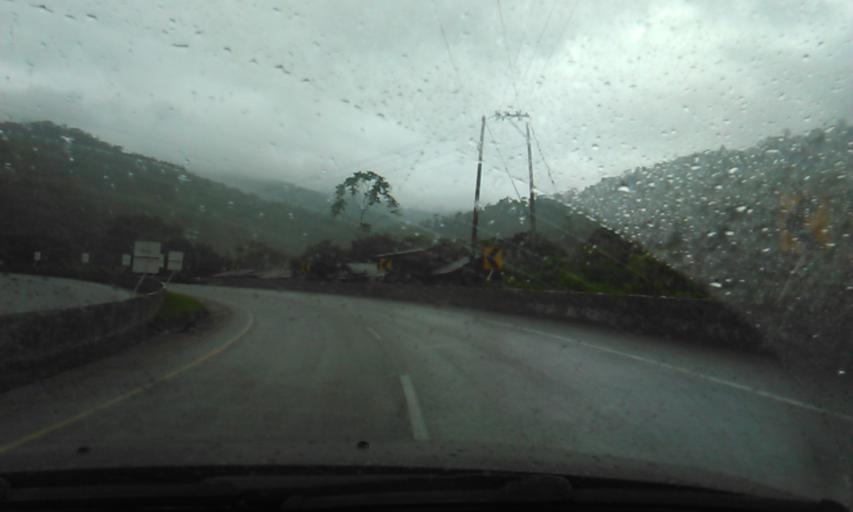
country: CO
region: Valle del Cauca
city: Buenaventura
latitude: 3.8656
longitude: -76.8256
